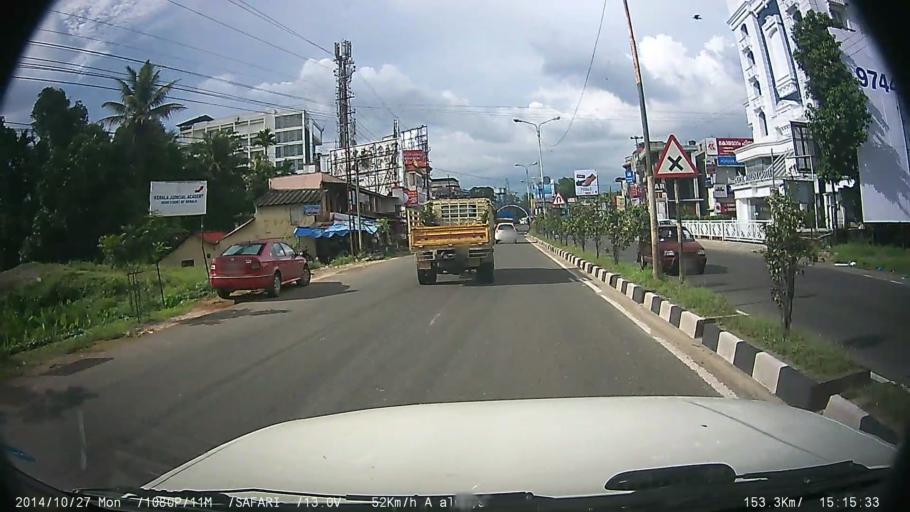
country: IN
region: Kerala
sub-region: Ernakulam
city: Aluva
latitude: 10.1543
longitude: 76.3546
